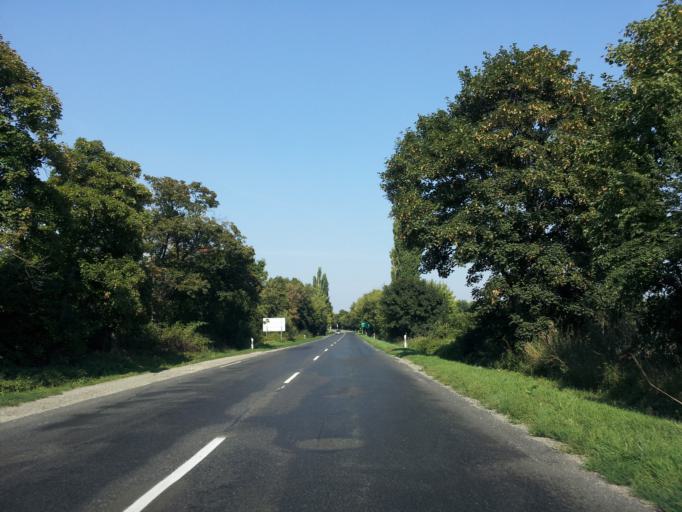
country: HU
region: Fejer
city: Lepseny
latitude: 46.9670
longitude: 18.2002
